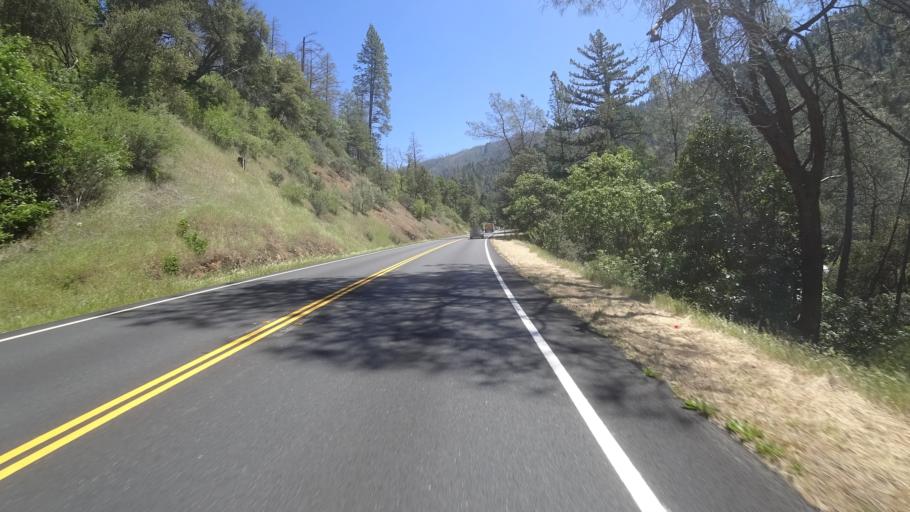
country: US
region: California
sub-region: Humboldt County
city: Willow Creek
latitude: 40.7874
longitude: -123.4280
